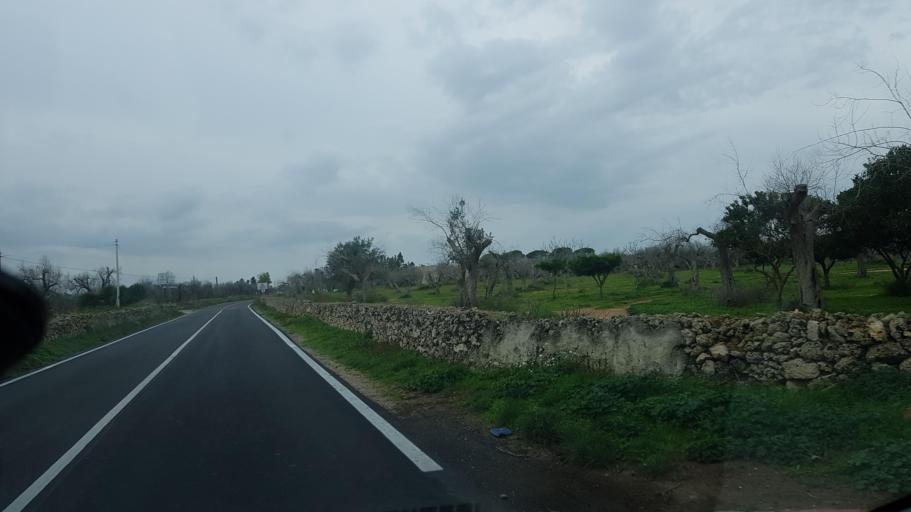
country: IT
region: Apulia
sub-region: Provincia di Lecce
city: Squinzano
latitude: 40.4537
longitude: 18.0520
